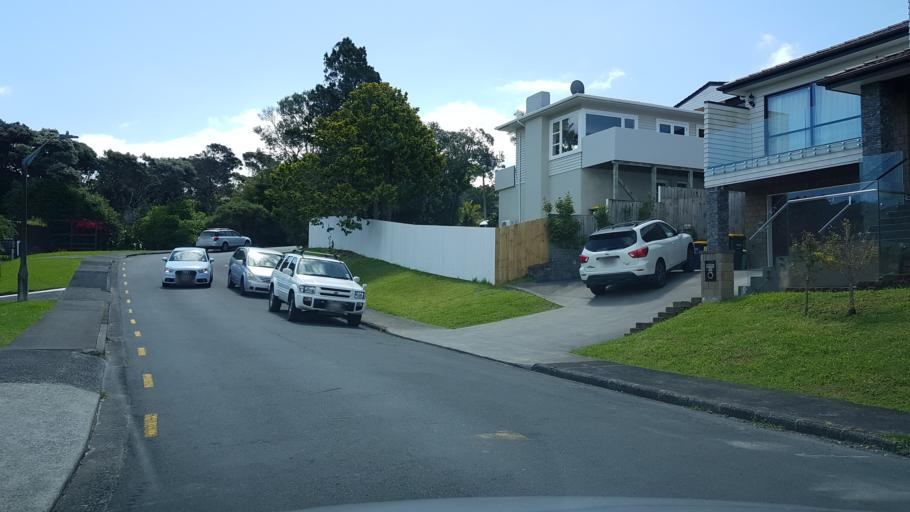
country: NZ
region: Auckland
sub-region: Auckland
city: North Shore
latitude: -36.8123
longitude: 174.7337
